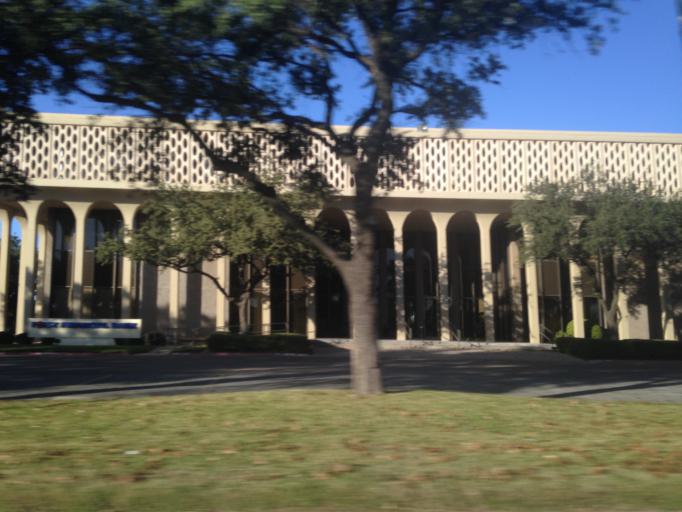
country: US
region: Texas
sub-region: Taylor County
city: Abilene
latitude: 32.4323
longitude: -99.7642
